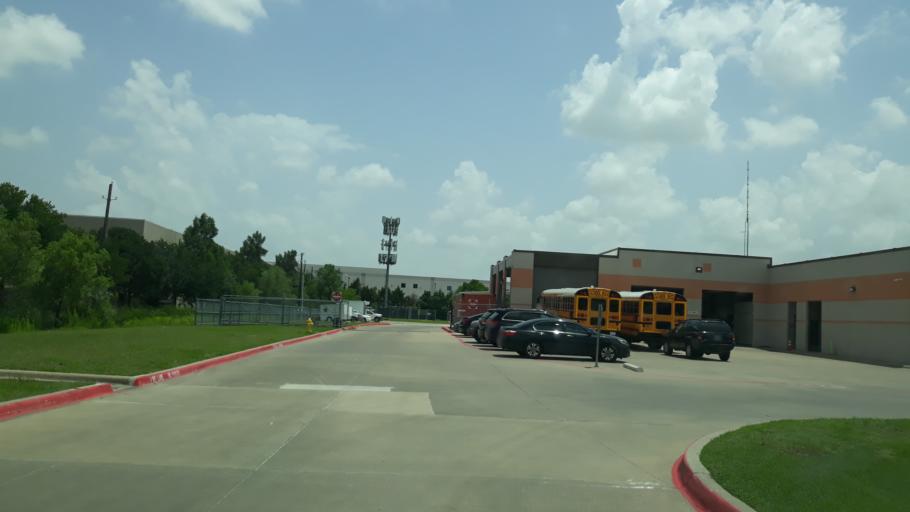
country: US
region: Texas
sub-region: Dallas County
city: Coppell
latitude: 32.9364
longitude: -97.0016
